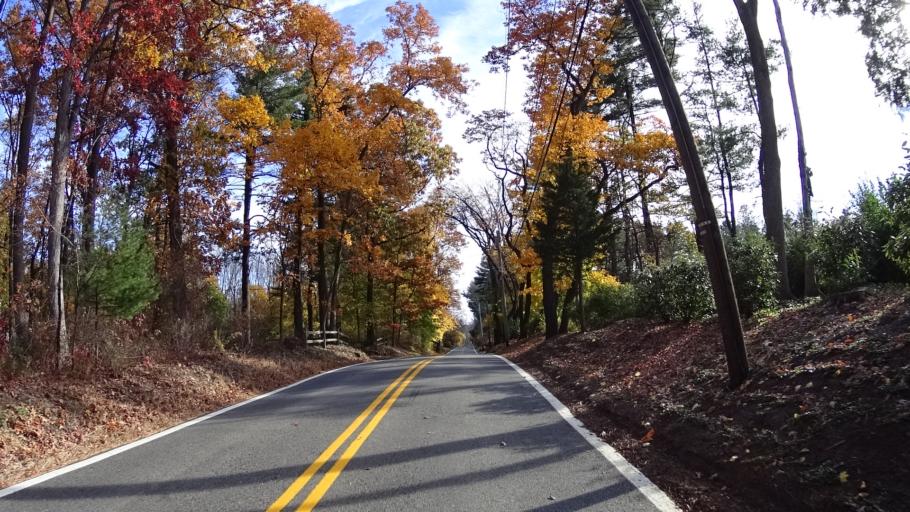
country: US
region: New Jersey
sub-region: Morris County
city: Morristown
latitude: 40.7387
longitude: -74.5007
